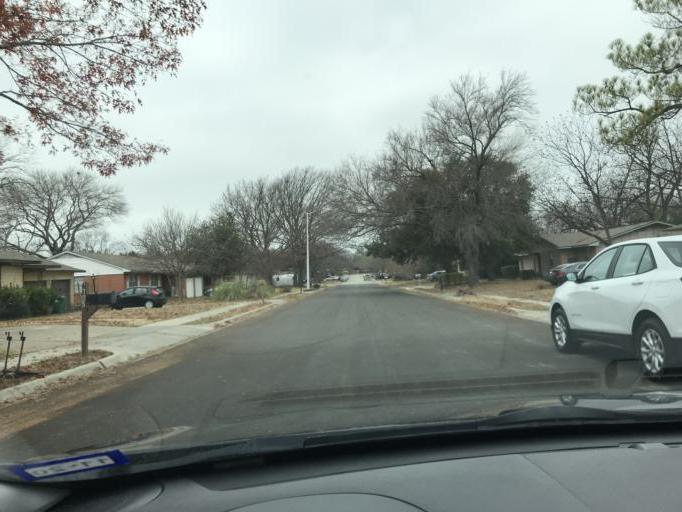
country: US
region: Texas
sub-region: Denton County
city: Denton
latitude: 33.2248
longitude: -97.1502
